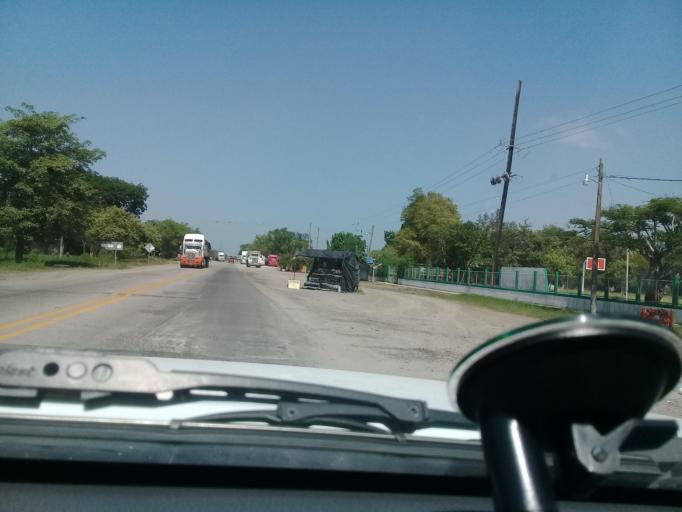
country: MX
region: Veracruz
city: Moralillo
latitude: 22.1716
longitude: -98.0512
